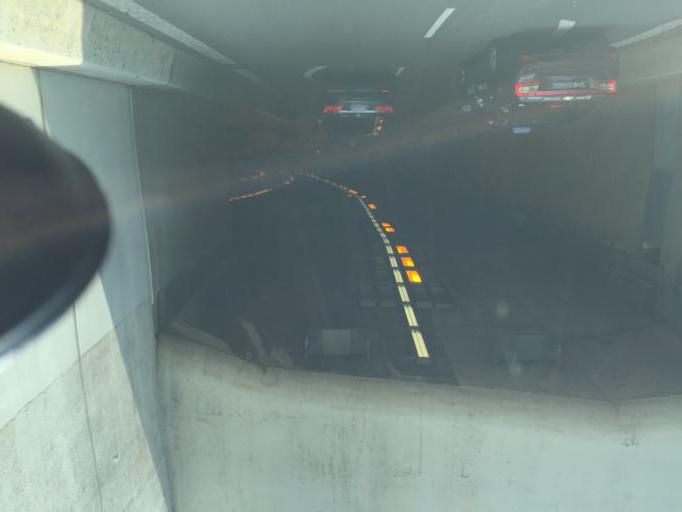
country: SG
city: Singapore
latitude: 1.3067
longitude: 103.8402
